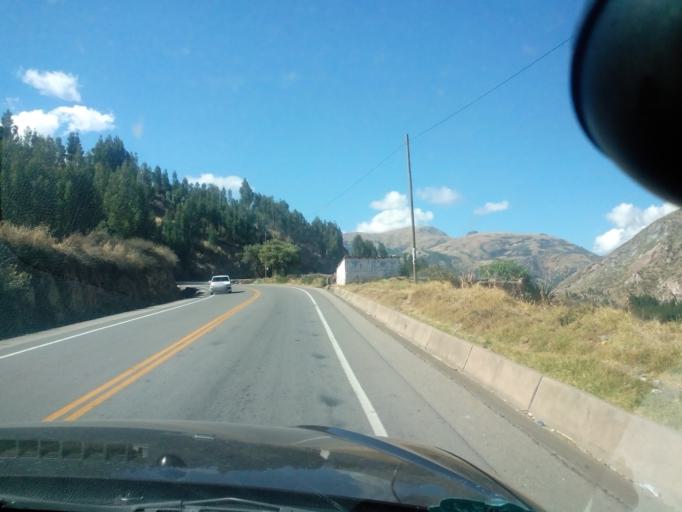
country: PE
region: Cusco
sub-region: Provincia de Quispicanchis
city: Urcos
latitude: -13.6858
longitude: -71.6122
